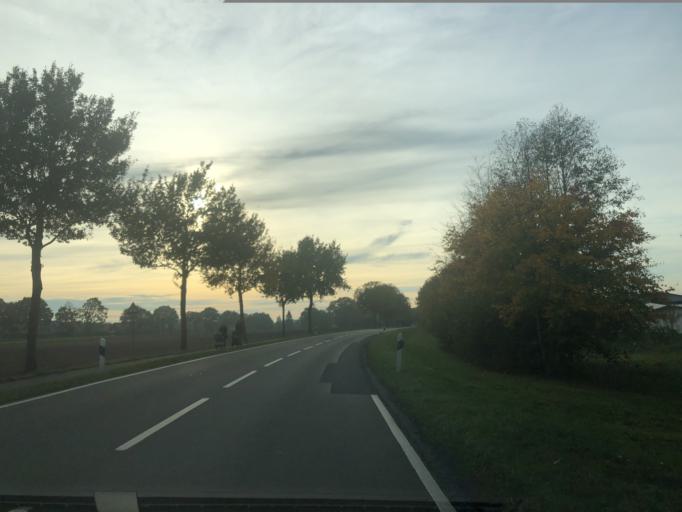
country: DE
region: Lower Saxony
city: Friesoythe
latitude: 53.0432
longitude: 7.8987
